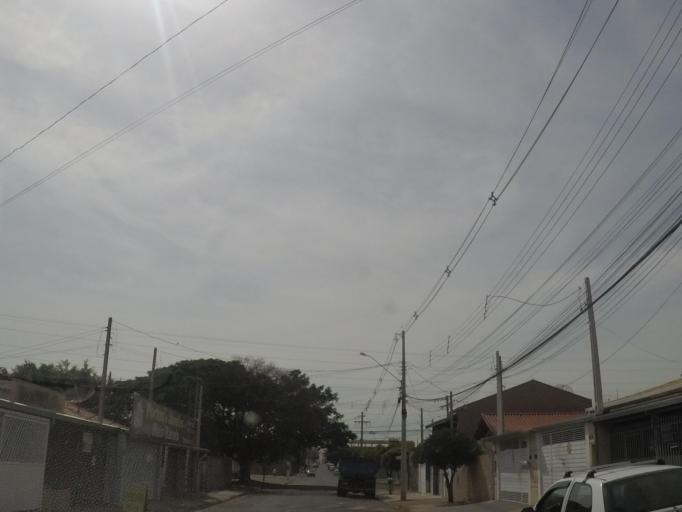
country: BR
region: Sao Paulo
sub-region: Hortolandia
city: Hortolandia
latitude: -22.8500
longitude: -47.1943
